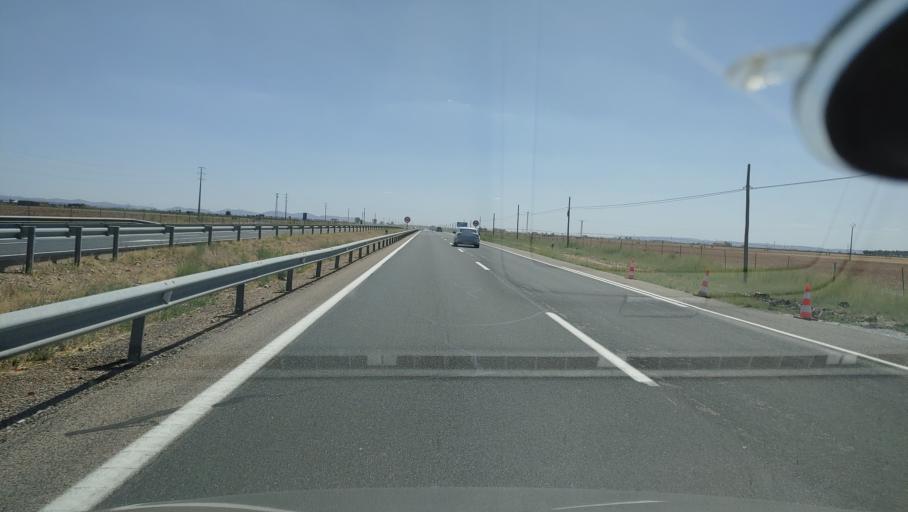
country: ES
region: Castille-La Mancha
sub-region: Provincia de Ciudad Real
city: Manzanares
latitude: 39.1010
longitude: -3.3770
